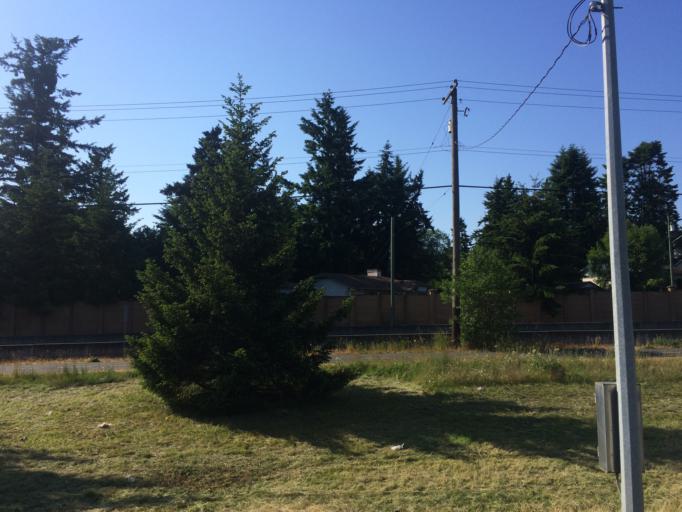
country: CA
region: British Columbia
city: Colwood
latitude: 48.4625
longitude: -123.4519
